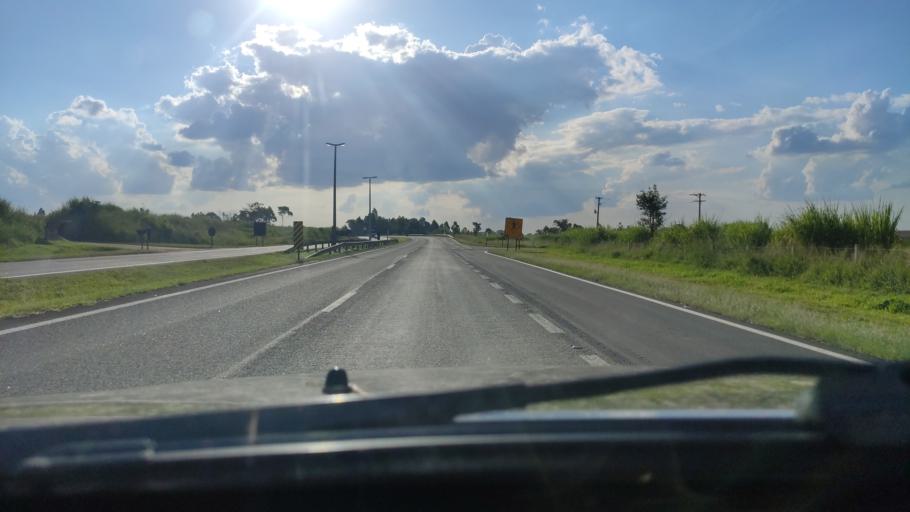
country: BR
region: Sao Paulo
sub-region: Itapira
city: Itapira
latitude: -22.4492
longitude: -46.8802
